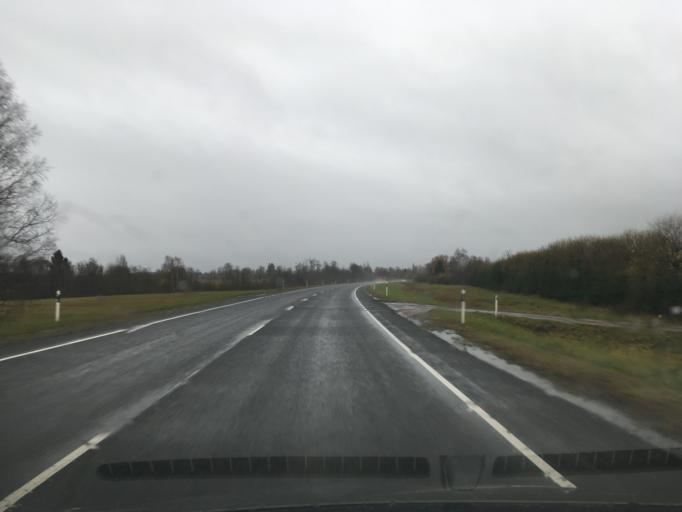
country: EE
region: Harju
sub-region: Nissi vald
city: Turba
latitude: 58.9230
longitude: 24.1121
